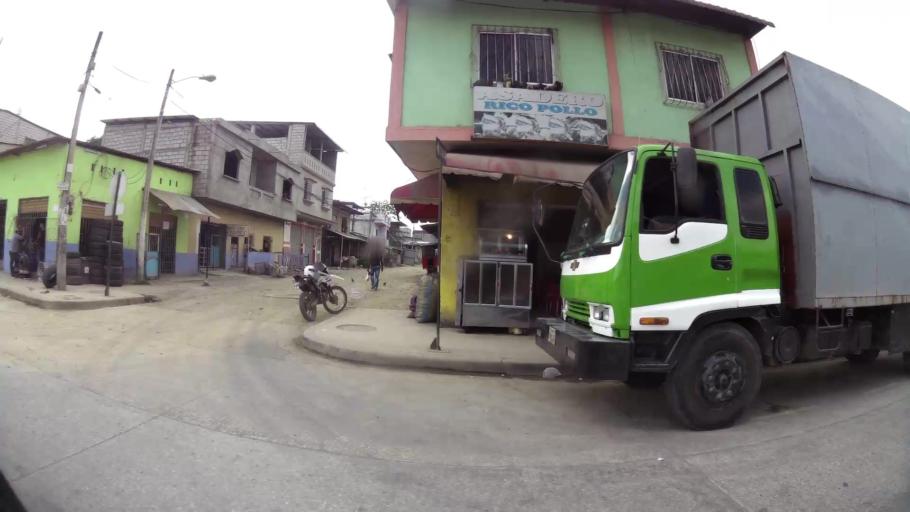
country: EC
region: Guayas
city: Santa Lucia
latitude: -2.1192
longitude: -79.9555
